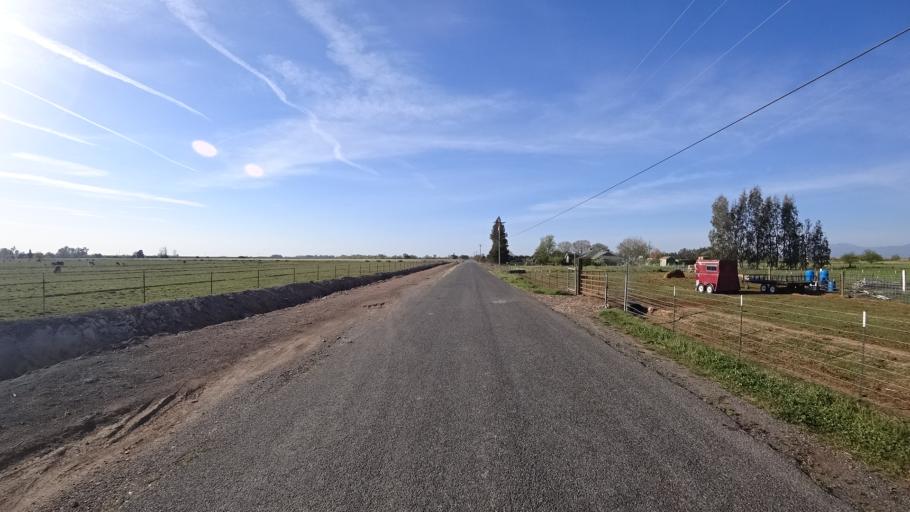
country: US
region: California
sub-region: Glenn County
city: Orland
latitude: 39.7170
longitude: -122.2347
